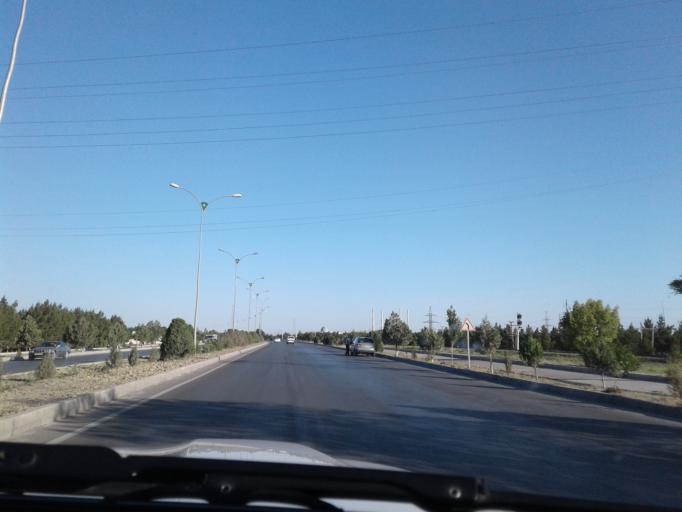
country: TM
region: Ahal
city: Abadan
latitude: 38.1536
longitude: 57.9772
